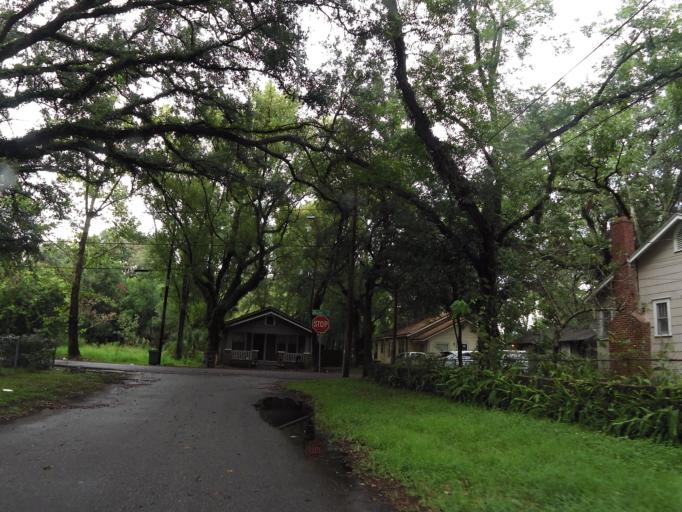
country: US
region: Florida
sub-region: Duval County
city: Jacksonville
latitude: 30.3232
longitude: -81.7111
